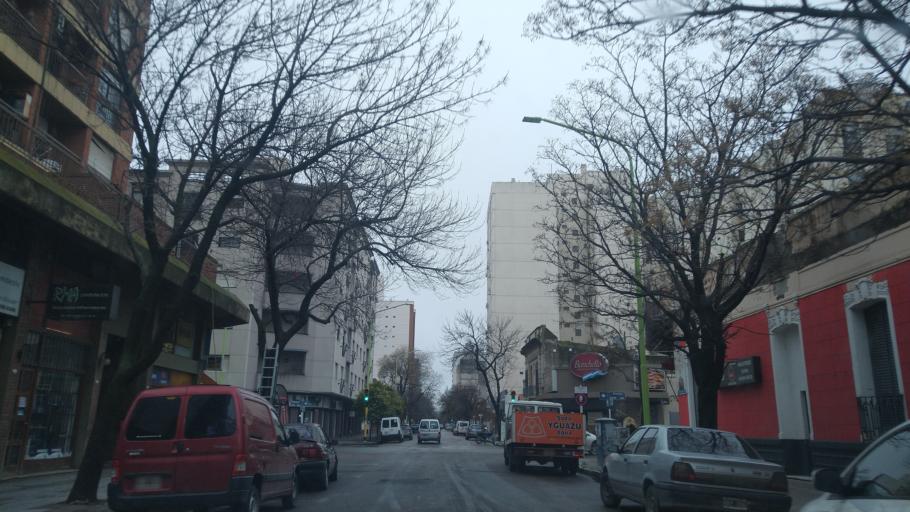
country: AR
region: Buenos Aires
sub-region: Partido de Bahia Blanca
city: Bahia Blanca
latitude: -38.7152
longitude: -62.2711
